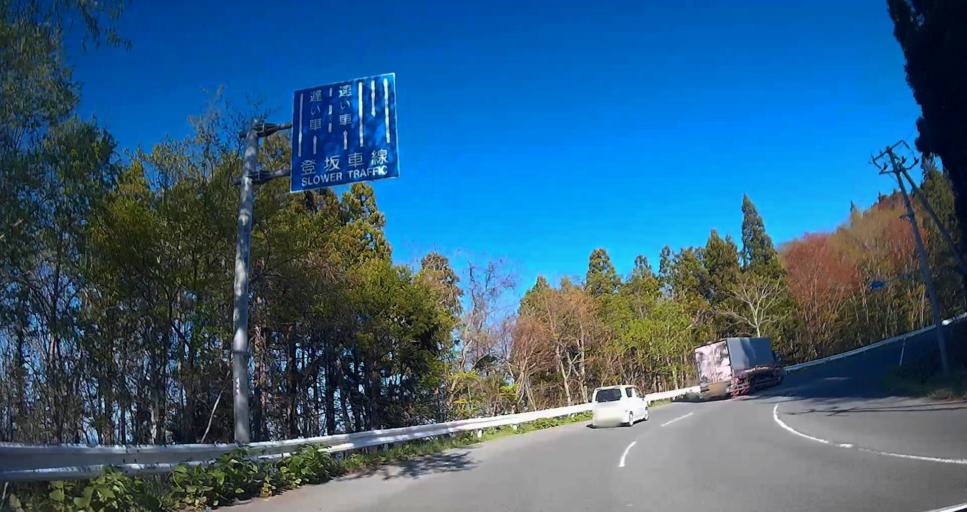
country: JP
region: Aomori
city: Mutsu
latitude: 41.4340
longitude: 141.1330
